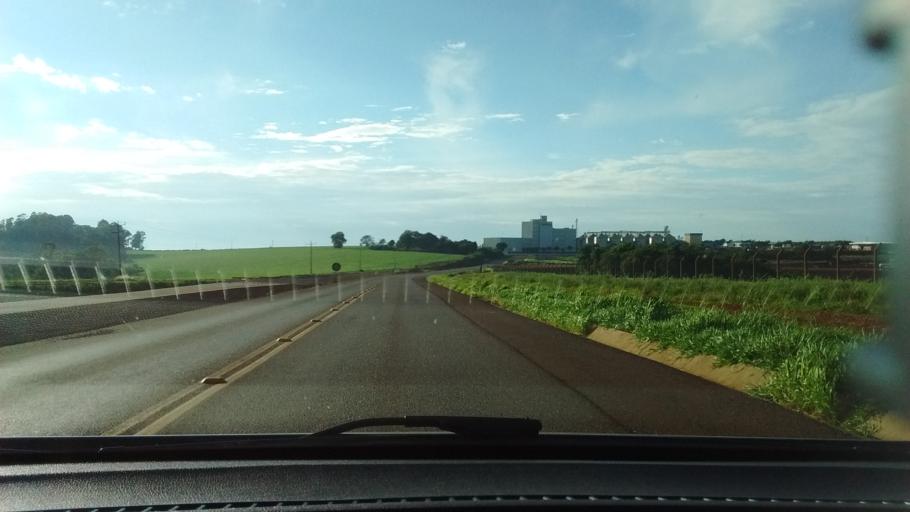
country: BR
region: Parana
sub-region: Cascavel
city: Cascavel
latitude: -25.1271
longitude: -53.5882
